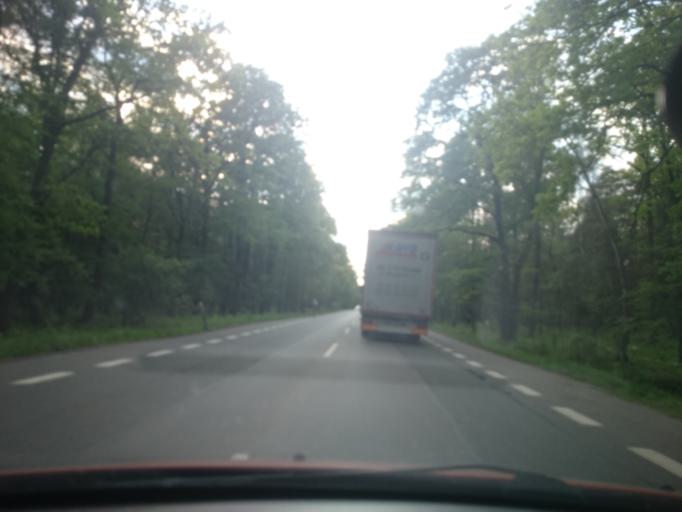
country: PL
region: Opole Voivodeship
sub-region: Powiat opolski
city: Chrzastowice
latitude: 50.6331
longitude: 18.0187
